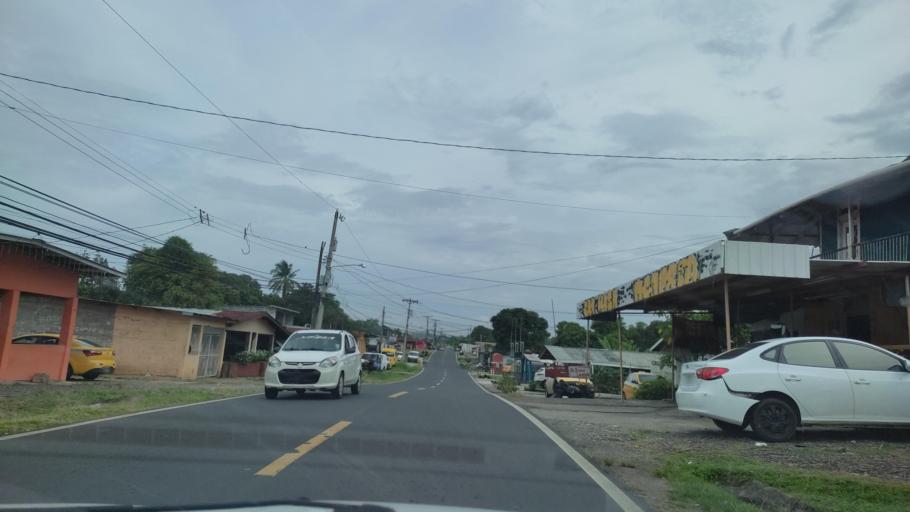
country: PA
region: Panama
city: San Miguelito
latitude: 9.0474
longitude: -79.4300
